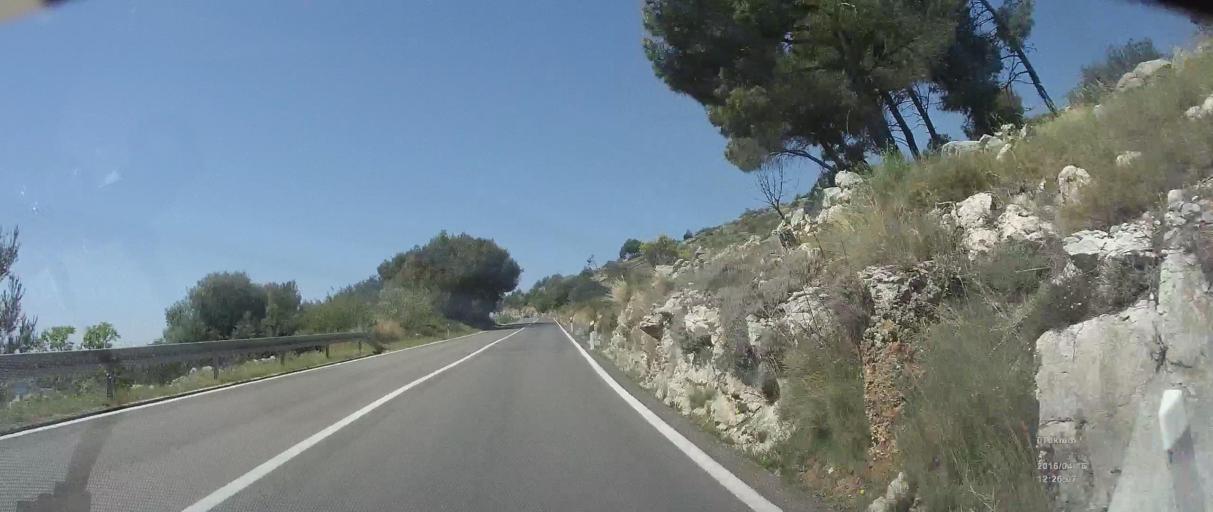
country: HR
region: Splitsko-Dalmatinska
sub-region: Grad Trogir
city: Trogir
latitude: 43.5173
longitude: 16.2129
